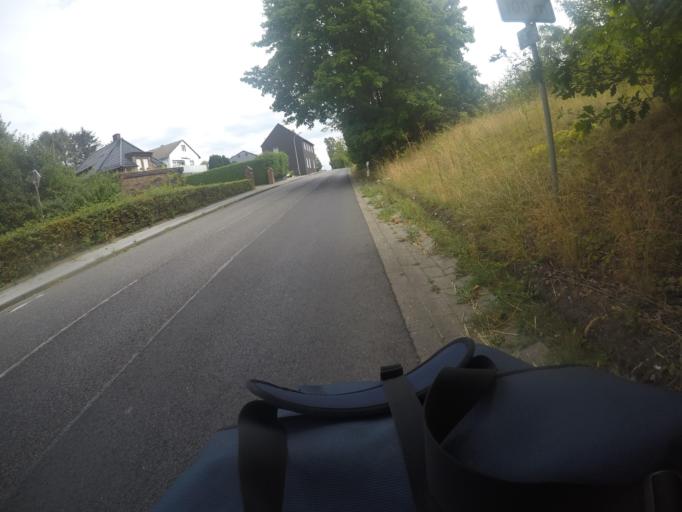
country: DE
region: North Rhine-Westphalia
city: Haan
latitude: 51.2114
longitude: 7.0141
